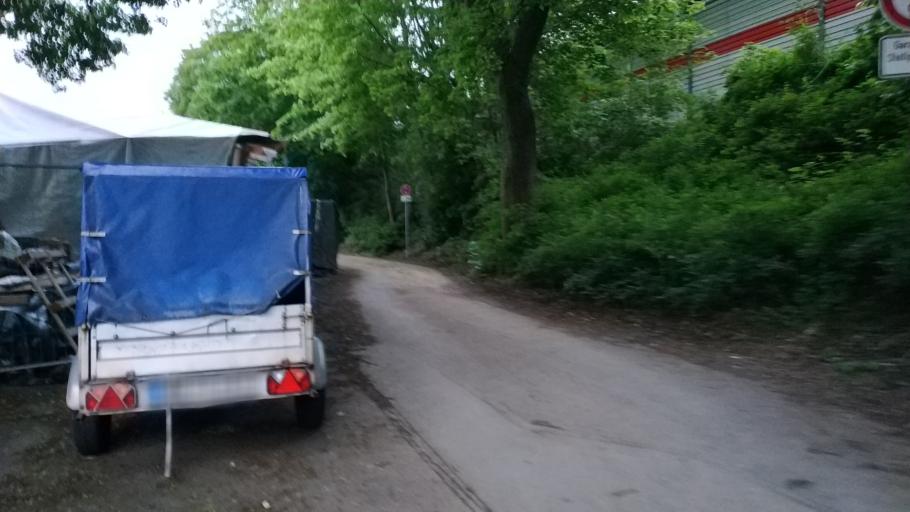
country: DE
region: Bavaria
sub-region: Regierungsbezirk Mittelfranken
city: Nuernberg
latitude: 49.4216
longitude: 11.0630
